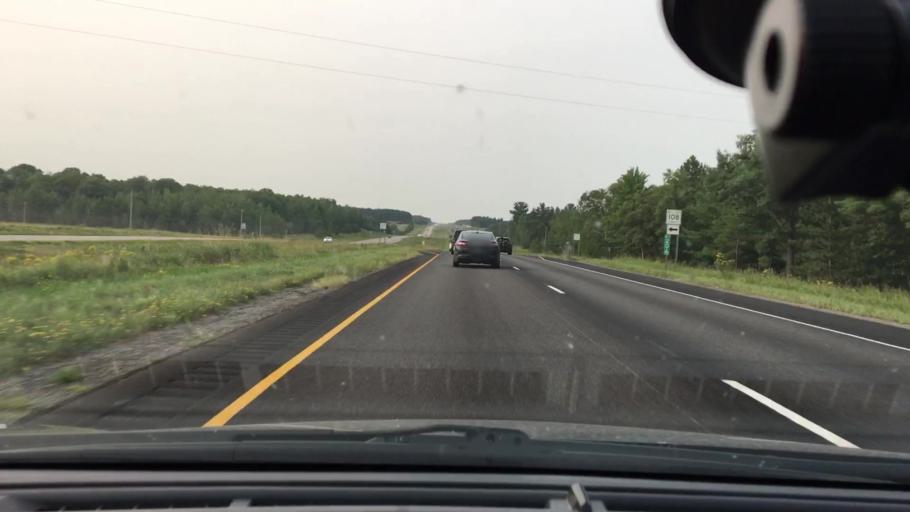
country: US
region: Minnesota
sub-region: Mille Lacs County
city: Milaca
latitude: 45.9640
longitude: -93.6613
